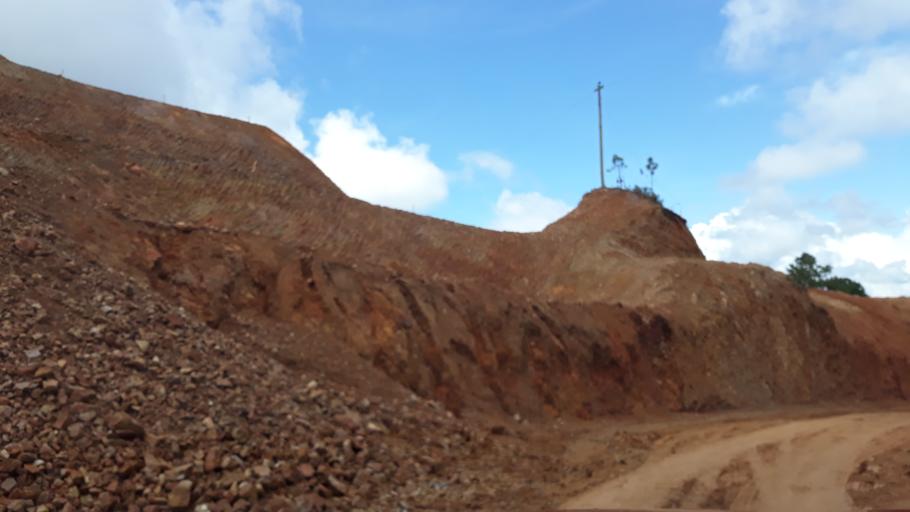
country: HN
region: El Paraiso
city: Santa Cruz
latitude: 13.7580
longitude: -86.6517
